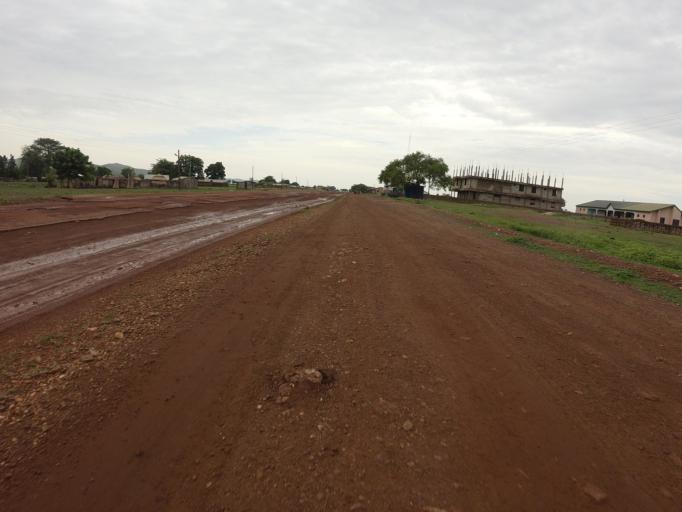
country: GH
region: Upper East
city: Bawku
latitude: 10.9279
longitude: -0.5045
